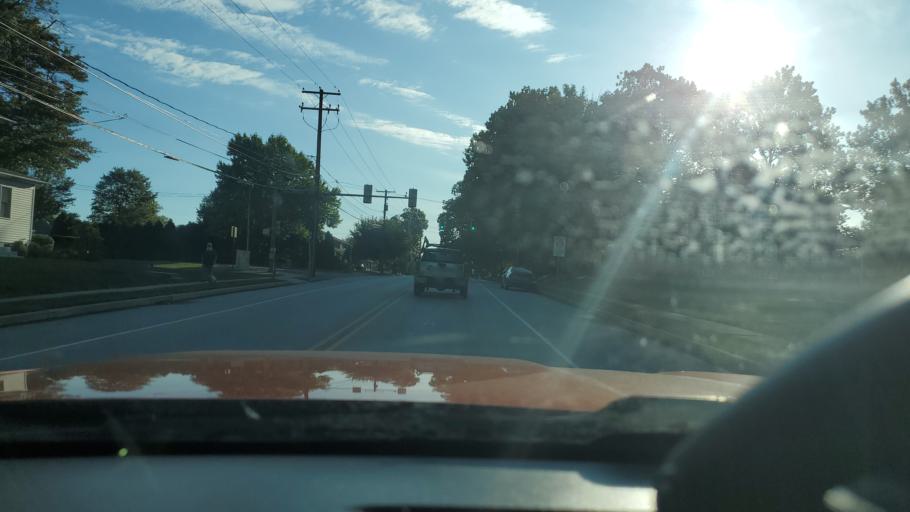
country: US
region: Pennsylvania
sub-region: Montgomery County
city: Telford
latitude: 40.3151
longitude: -75.3358
